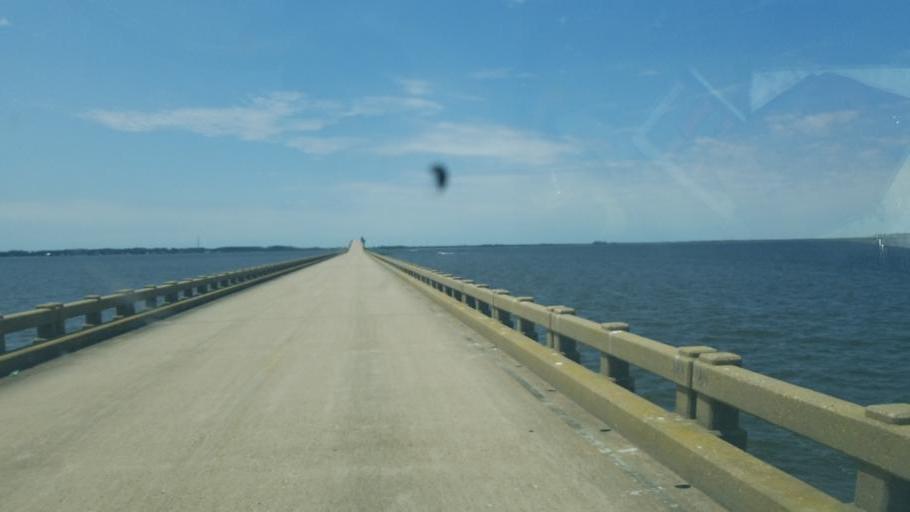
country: US
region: North Carolina
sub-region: Dare County
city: Manteo
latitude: 35.9214
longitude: -75.7407
